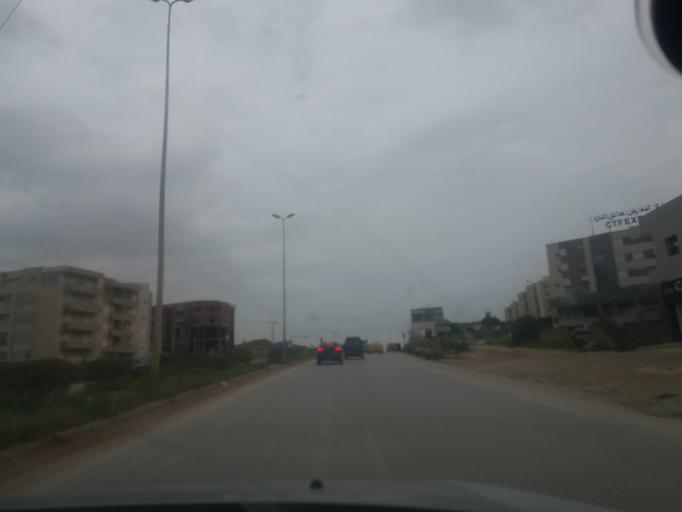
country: TN
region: Tunis
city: Tunis
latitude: 36.8556
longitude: 10.1306
